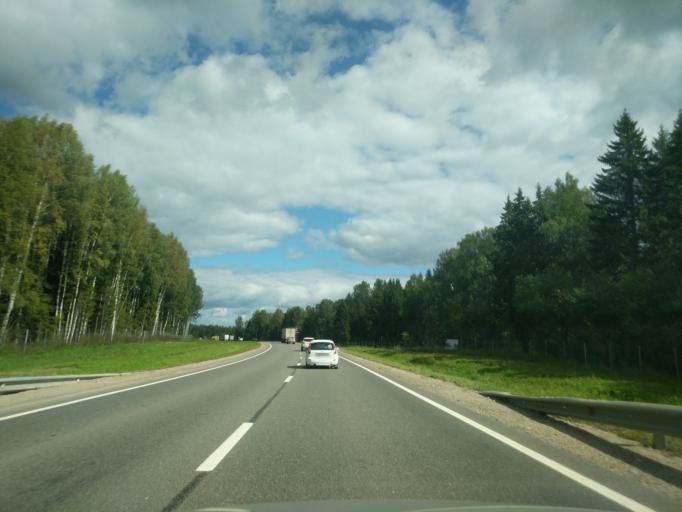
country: RU
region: Kostroma
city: Oktyabr'skiy
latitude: 57.7986
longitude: 41.2606
